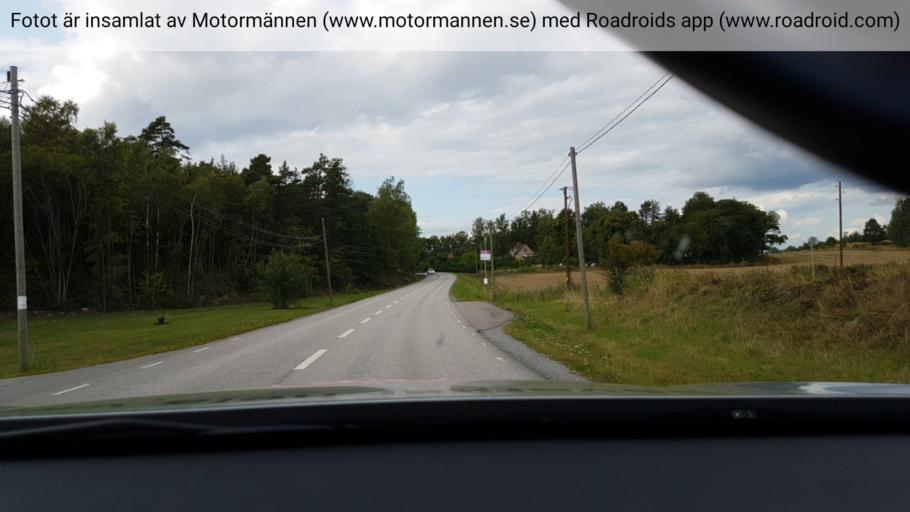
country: SE
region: Stockholm
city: Stenhamra
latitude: 59.3817
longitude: 17.6876
